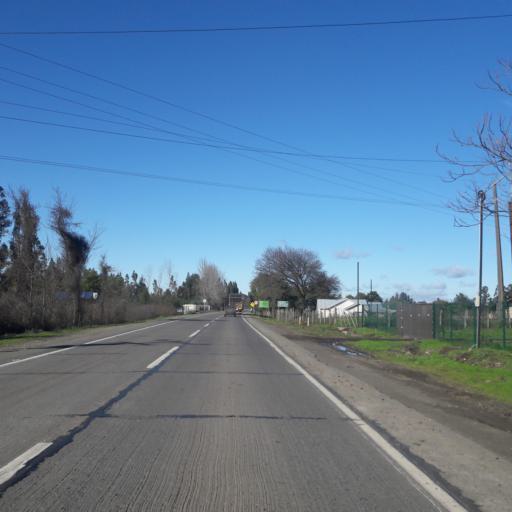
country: CL
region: Araucania
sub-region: Provincia de Malleco
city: Angol
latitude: -37.7384
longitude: -72.6132
